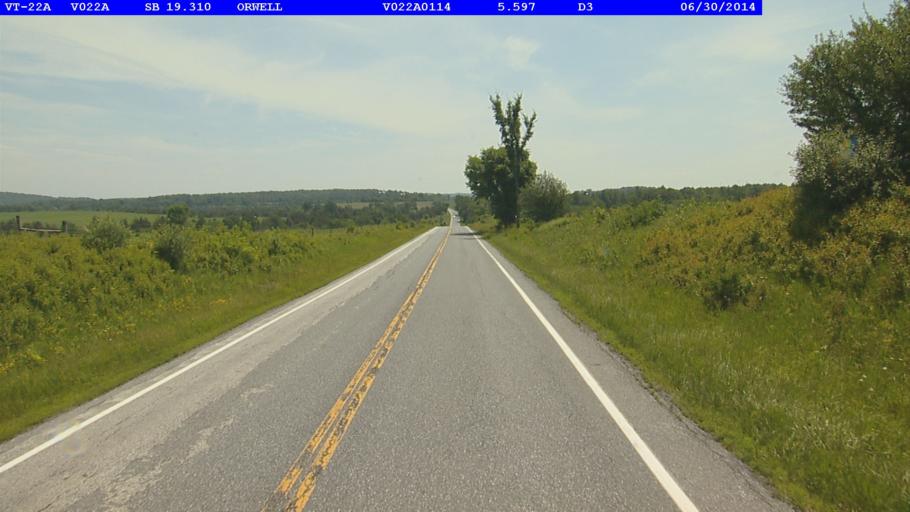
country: US
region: New York
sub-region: Essex County
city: Ticonderoga
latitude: 43.8374
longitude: -73.3099
